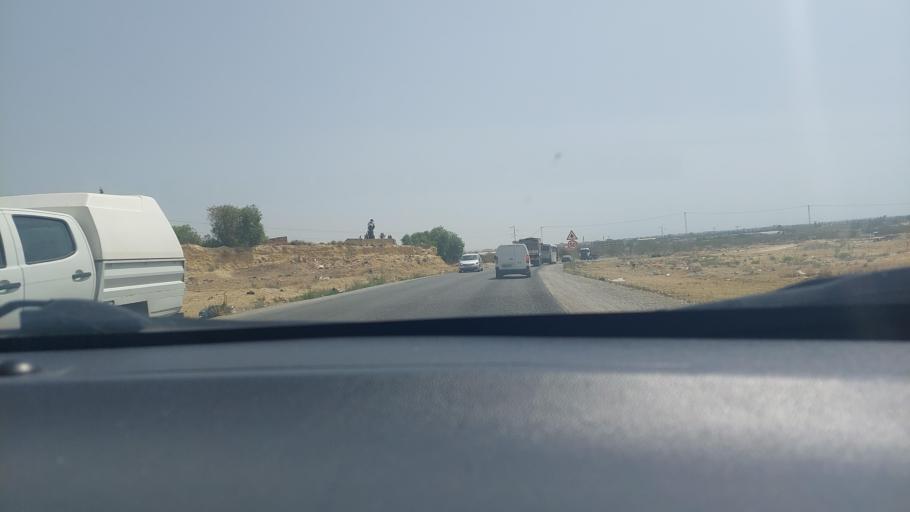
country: TN
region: Al Munastir
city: Qasr Hallal
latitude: 35.6365
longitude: 10.8695
